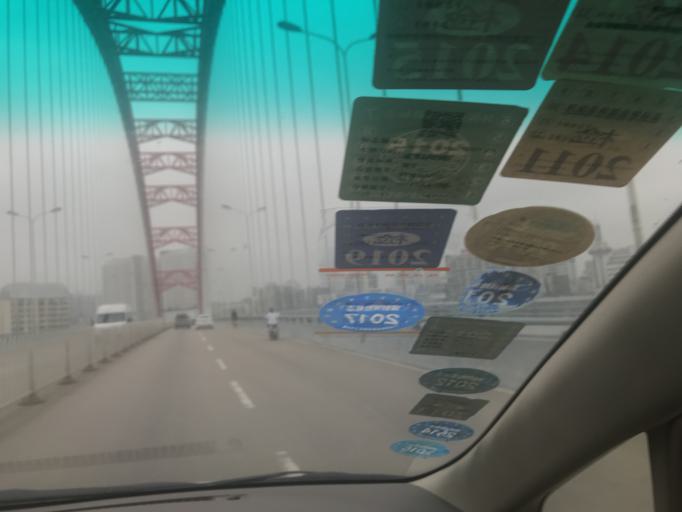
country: CN
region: Hubei
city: Wuhan
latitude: 30.5651
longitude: 114.2800
